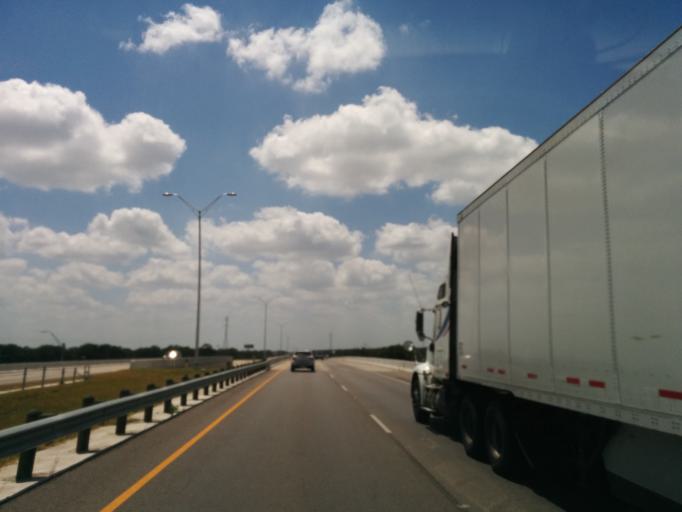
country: US
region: Texas
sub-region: Bastrop County
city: Bastrop
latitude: 30.1111
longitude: -97.3719
